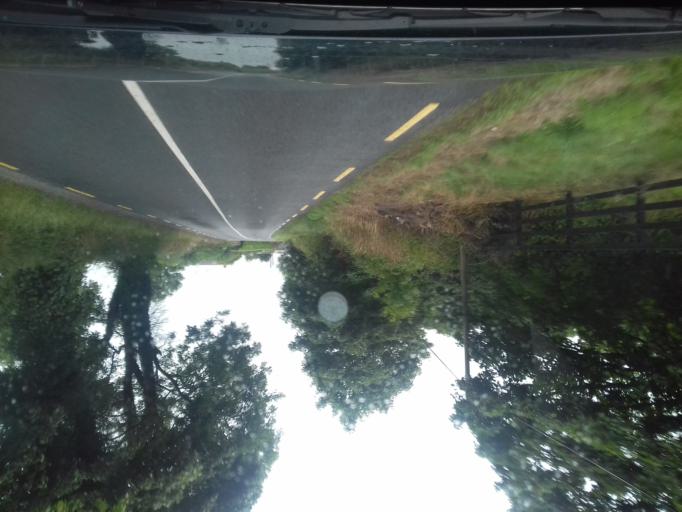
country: IE
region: Leinster
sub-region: Kilkenny
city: Graiguenamanagh
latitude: 52.6149
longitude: -6.9369
